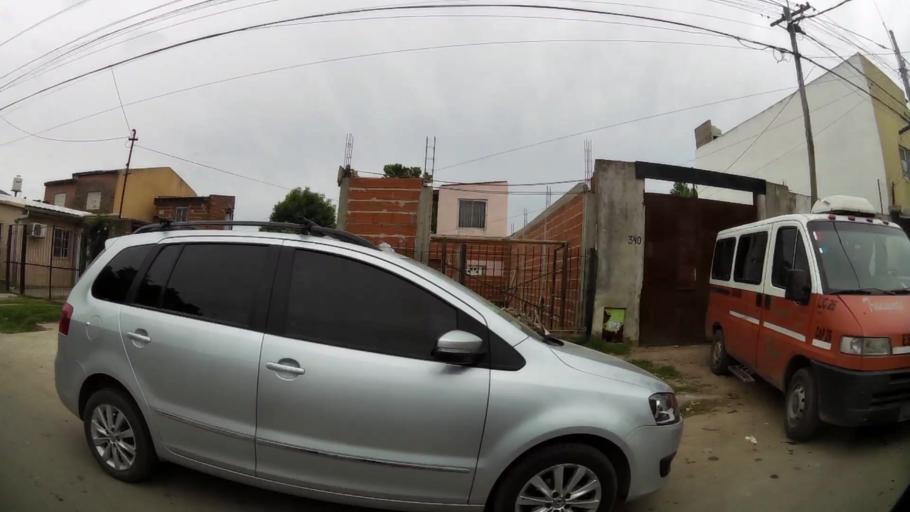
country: AR
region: Buenos Aires
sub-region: Partido de Campana
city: Campana
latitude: -34.1833
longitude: -58.9383
